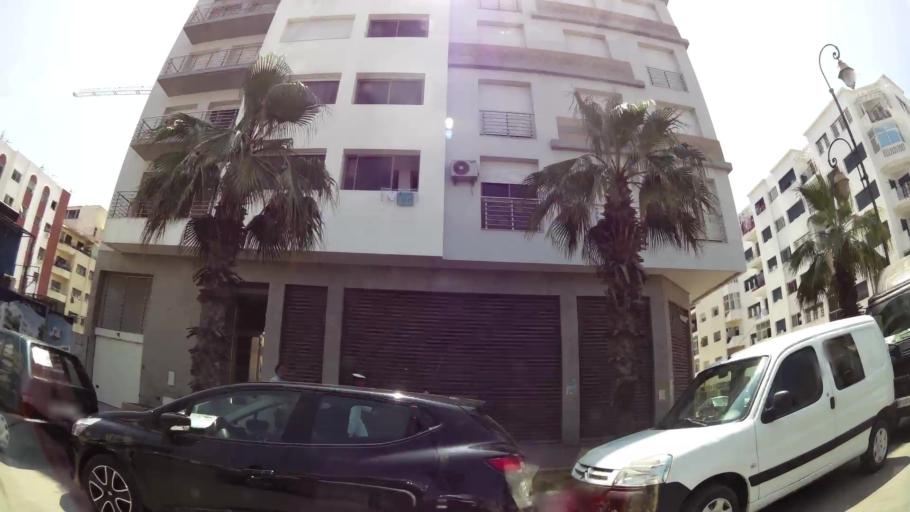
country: MA
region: Rabat-Sale-Zemmour-Zaer
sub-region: Rabat
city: Rabat
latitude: 34.0231
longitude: -6.8458
